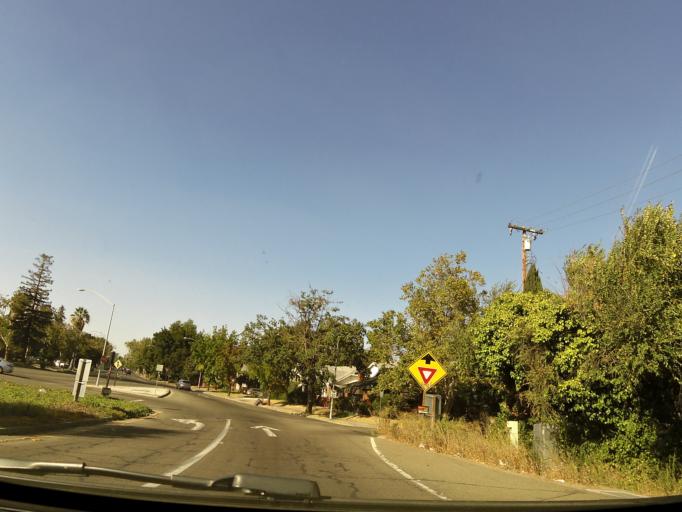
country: US
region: California
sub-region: San Joaquin County
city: Stockton
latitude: 37.9570
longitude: -121.3115
